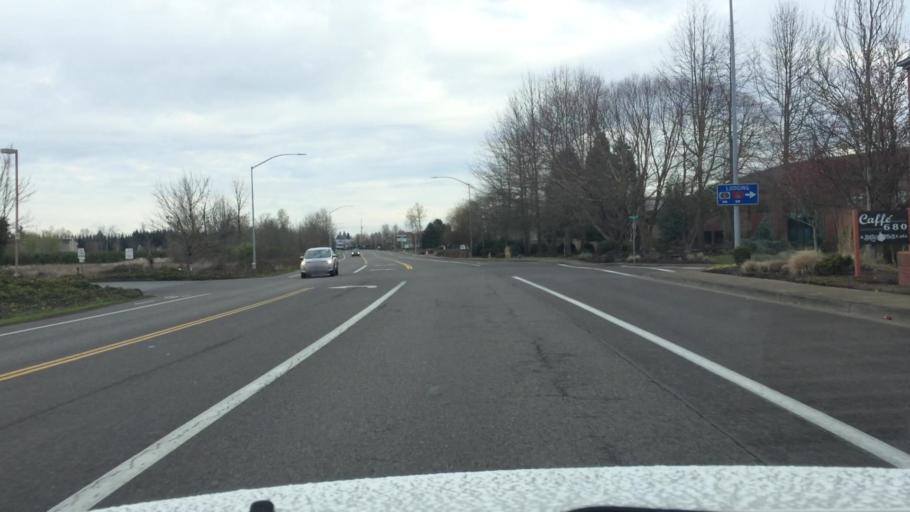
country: US
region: Oregon
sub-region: Marion County
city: Four Corners
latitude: 44.9224
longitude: -122.9951
